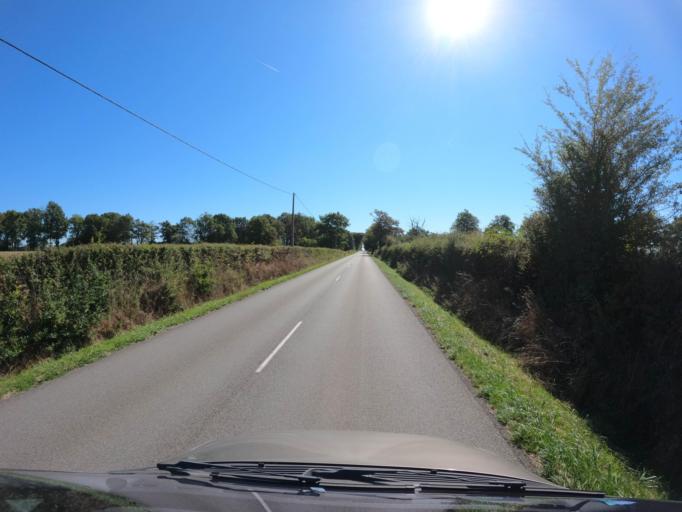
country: FR
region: Limousin
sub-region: Departement de la Haute-Vienne
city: Le Dorat
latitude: 46.2682
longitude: 1.0274
